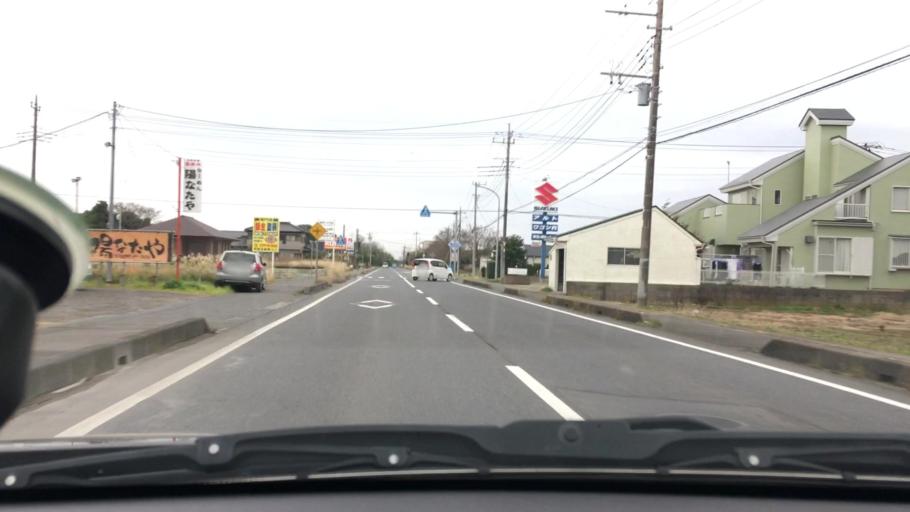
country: JP
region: Chiba
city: Omigawa
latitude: 35.8677
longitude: 140.6636
